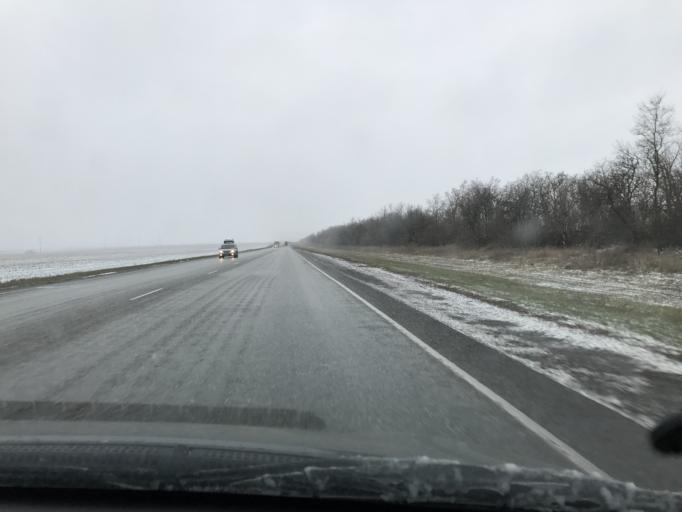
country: RU
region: Rostov
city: Mechetinskaya
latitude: 46.6880
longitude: 40.5161
